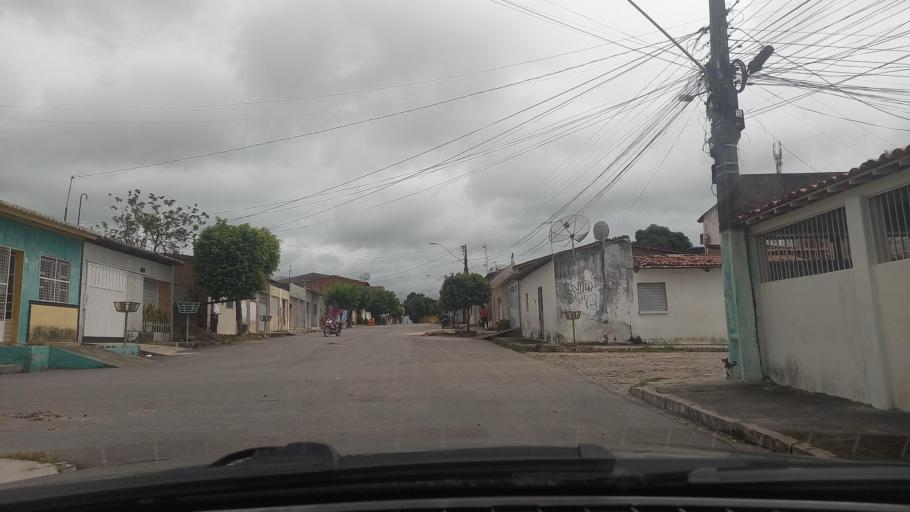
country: BR
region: Alagoas
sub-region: Delmiro Gouveia
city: Delmiro Gouveia
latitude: -9.3913
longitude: -37.9963
